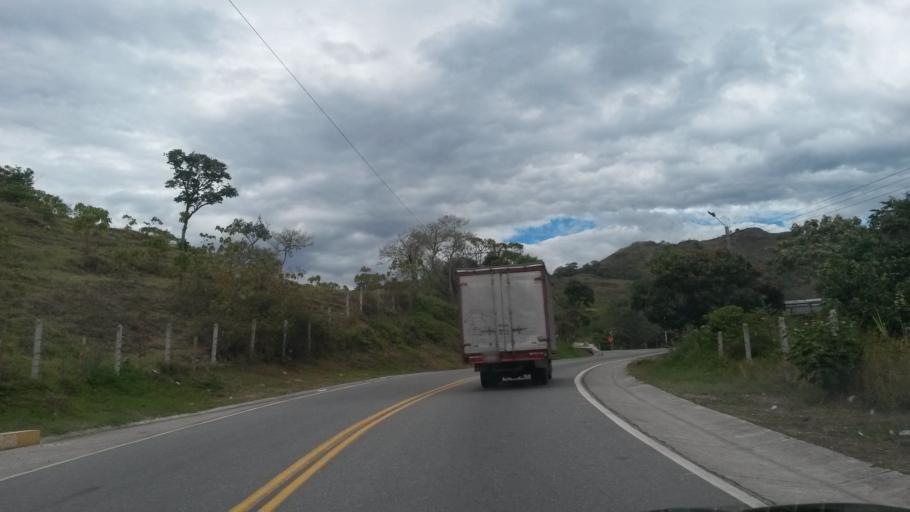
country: CO
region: Cauca
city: Rosas
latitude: 2.2625
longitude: -76.7445
